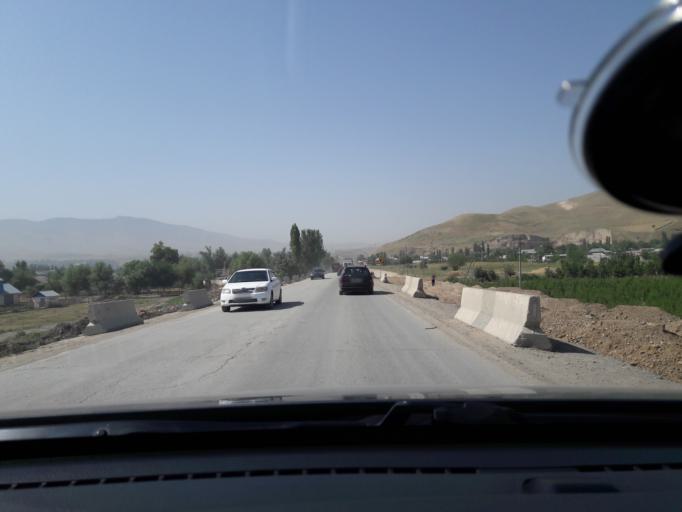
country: TJ
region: Dushanbe
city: Boshkengash
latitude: 38.4504
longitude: 68.7345
